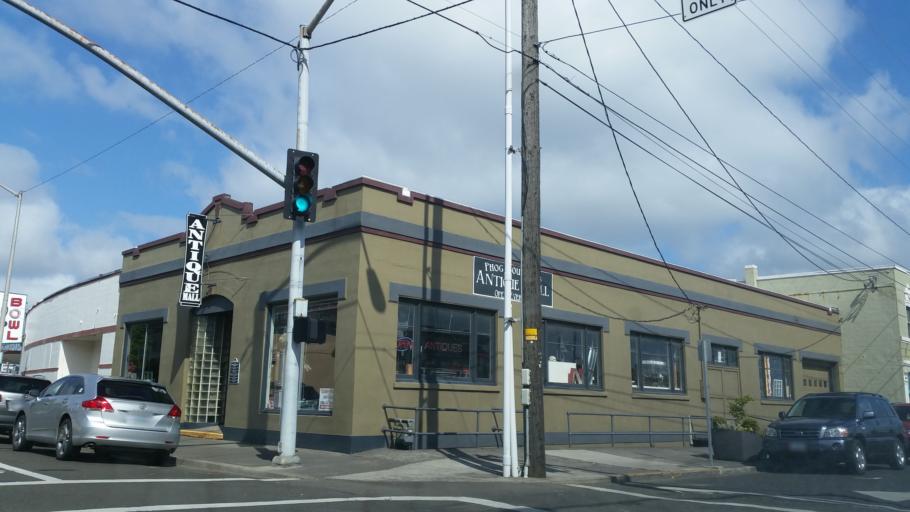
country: US
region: Oregon
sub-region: Clatsop County
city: Astoria
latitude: 46.1898
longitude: -123.8336
